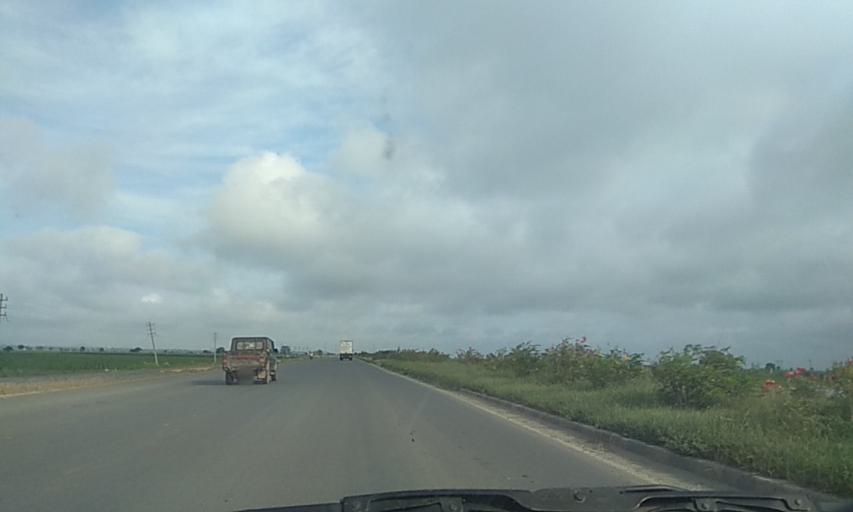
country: IN
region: Karnataka
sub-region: Haveri
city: Savanur
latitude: 14.8883
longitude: 75.3017
